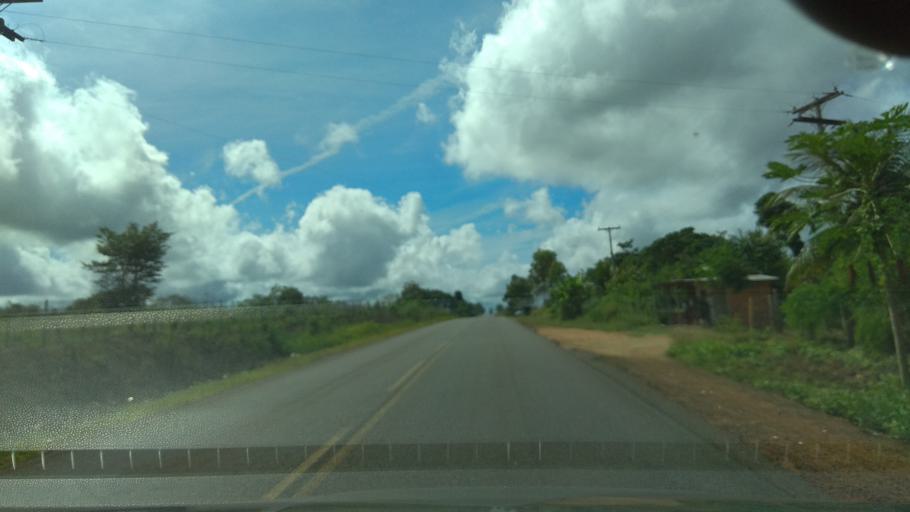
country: BR
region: Bahia
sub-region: Mutuipe
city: Mutuipe
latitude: -13.1730
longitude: -39.3574
